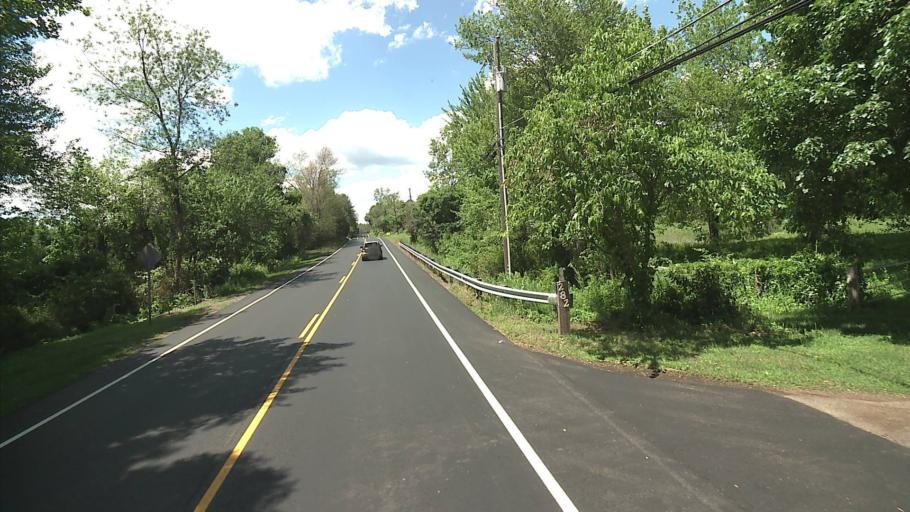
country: US
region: Connecticut
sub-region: Tolland County
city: Somers
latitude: 42.0016
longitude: -72.4345
